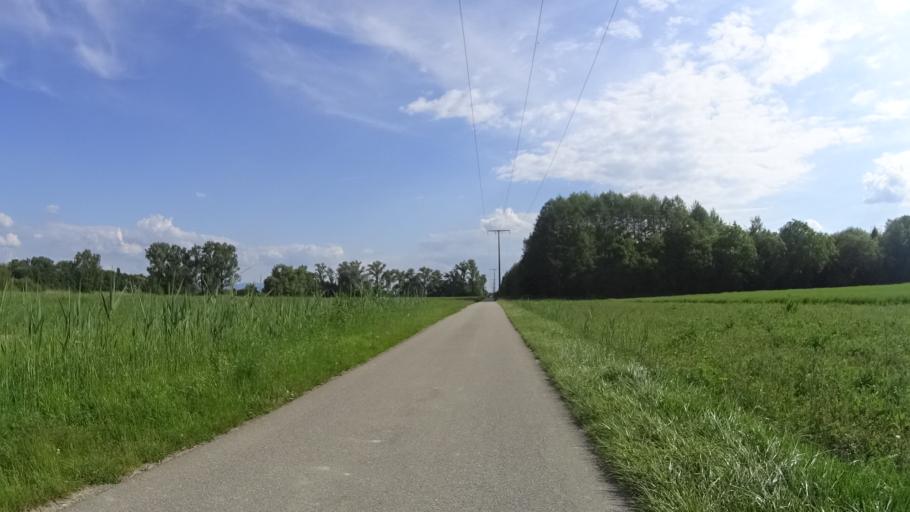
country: DE
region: Baden-Wuerttemberg
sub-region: Freiburg Region
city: Breisach am Rhein
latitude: 48.0730
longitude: 7.5912
